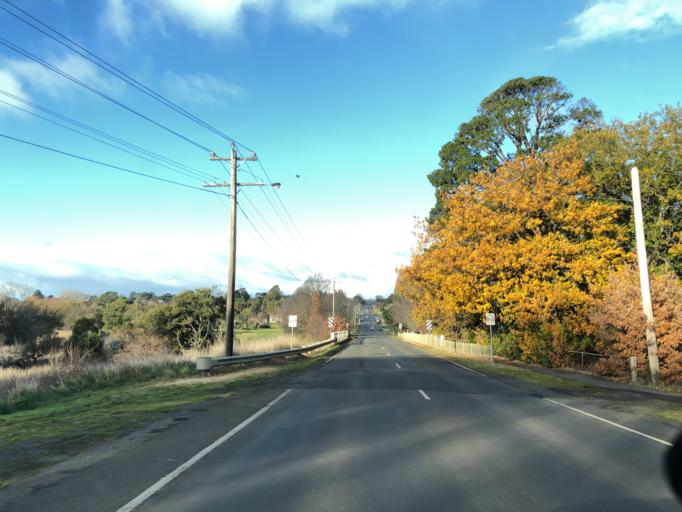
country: AU
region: Victoria
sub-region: Mount Alexander
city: Castlemaine
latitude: -37.1880
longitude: 144.3782
